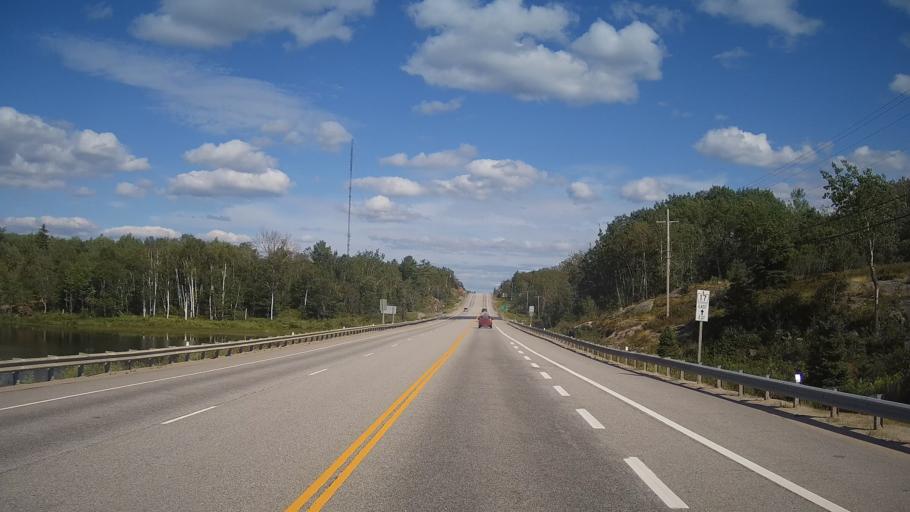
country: CA
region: Ontario
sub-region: Nipissing District
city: North Bay
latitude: 46.3041
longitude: -79.4227
